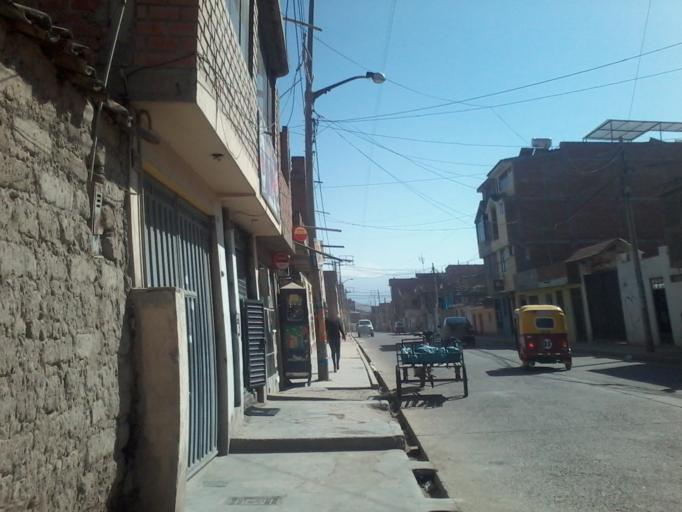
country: PE
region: Ayacucho
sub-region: Provincia de Huamanga
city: Ayacucho
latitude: -13.1668
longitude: -74.2115
